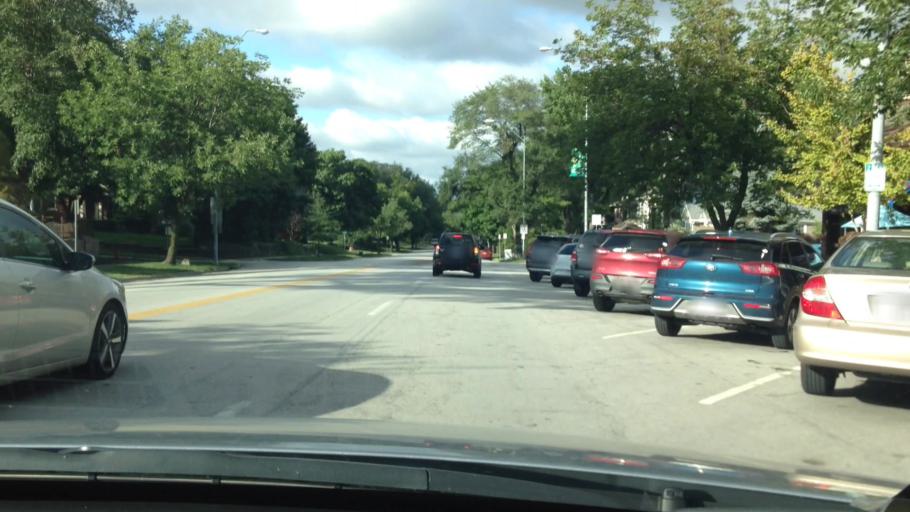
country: US
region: Kansas
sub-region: Johnson County
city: Mission Hills
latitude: 39.0144
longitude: -94.5913
